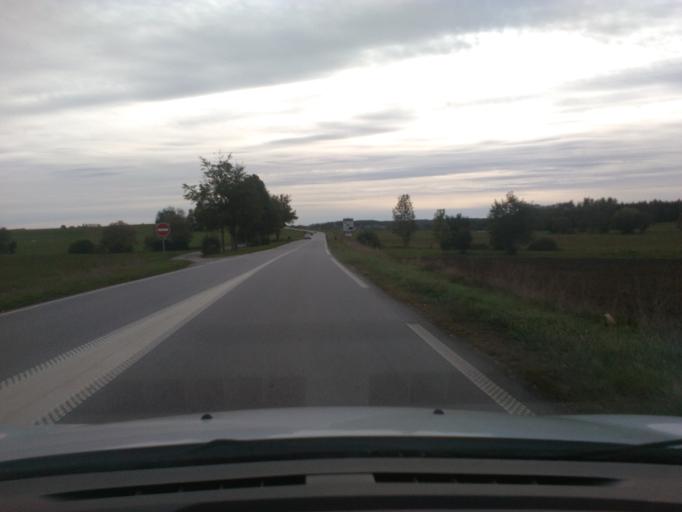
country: FR
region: Lorraine
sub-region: Departement des Vosges
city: Rambervillers
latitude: 48.3008
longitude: 6.5979
